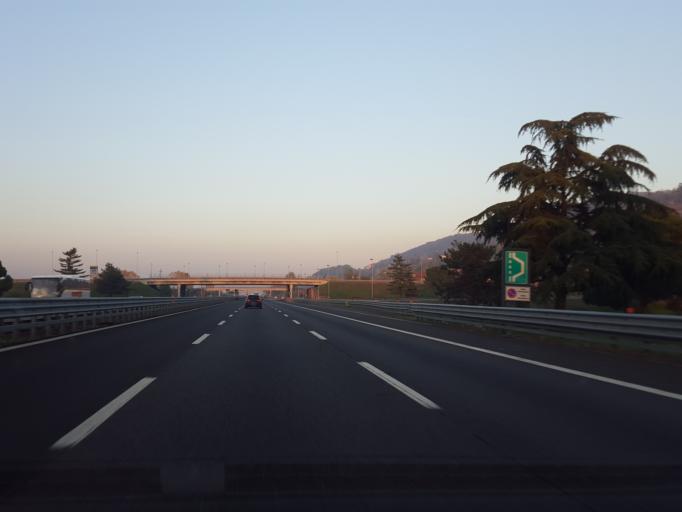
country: IT
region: Veneto
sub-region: Provincia di Vicenza
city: Brendola
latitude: 45.4885
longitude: 11.4401
